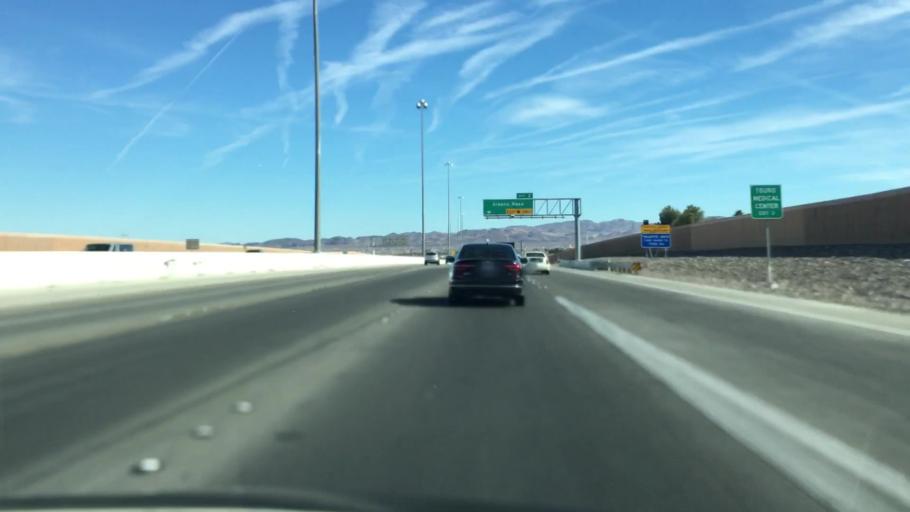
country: US
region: Nevada
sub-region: Clark County
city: Henderson
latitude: 36.0301
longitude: -115.0405
